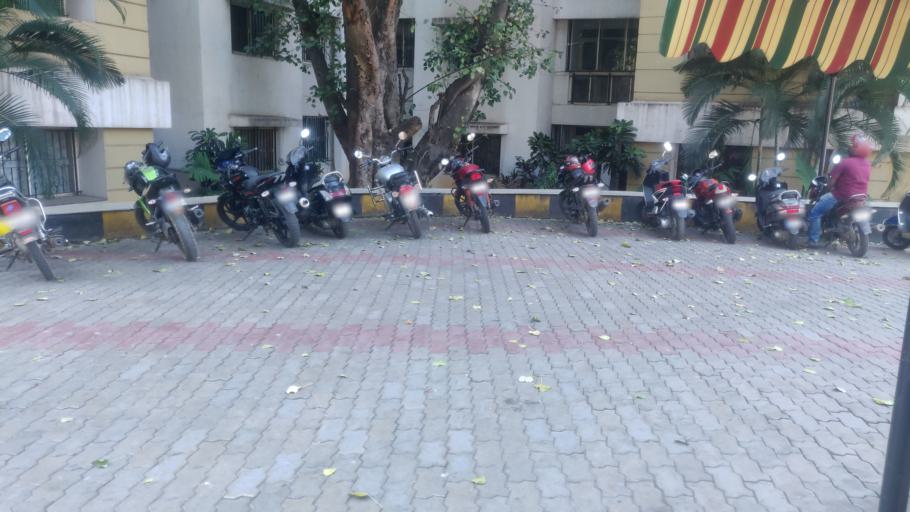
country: IN
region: Karnataka
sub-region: Bangalore Urban
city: Bangalore
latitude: 13.0135
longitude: 77.5513
